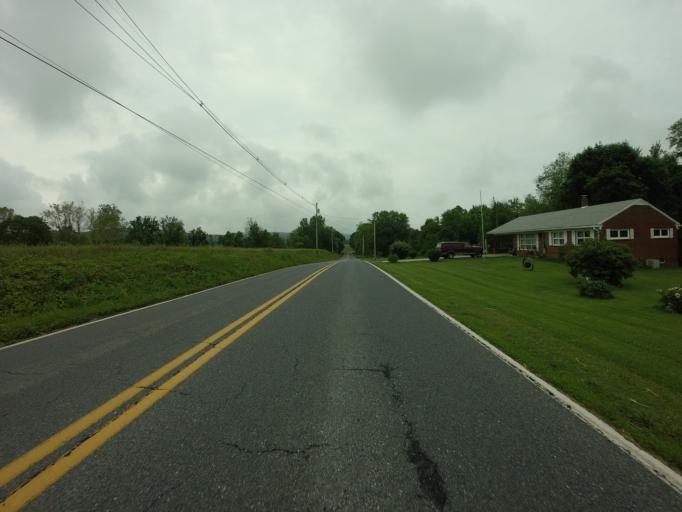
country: US
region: Maryland
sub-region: Frederick County
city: Jefferson
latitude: 39.3569
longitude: -77.5319
